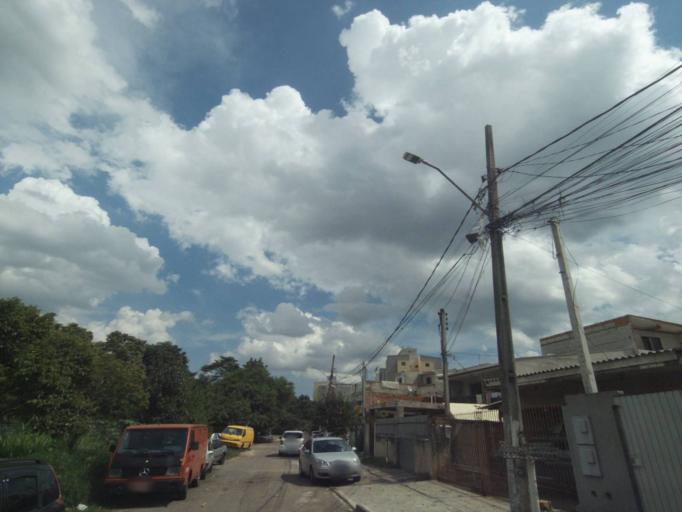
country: BR
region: Parana
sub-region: Curitiba
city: Curitiba
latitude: -25.4591
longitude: -49.3398
